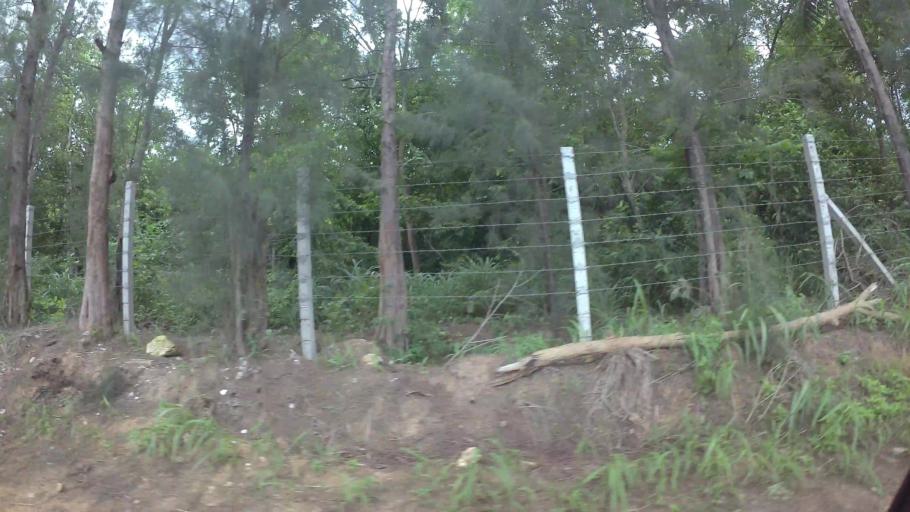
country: TH
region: Chon Buri
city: Si Racha
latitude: 13.1859
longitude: 100.9639
